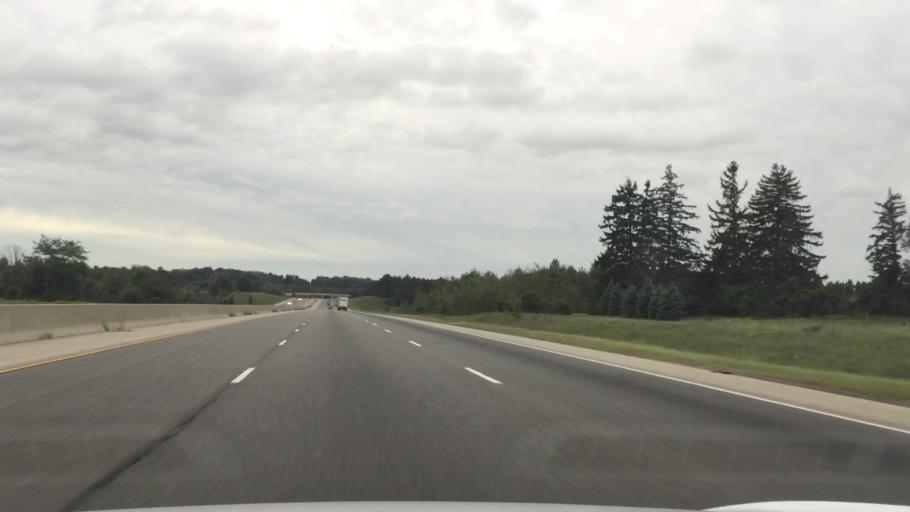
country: CA
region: Ontario
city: Kitchener
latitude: 43.3083
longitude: -80.4785
